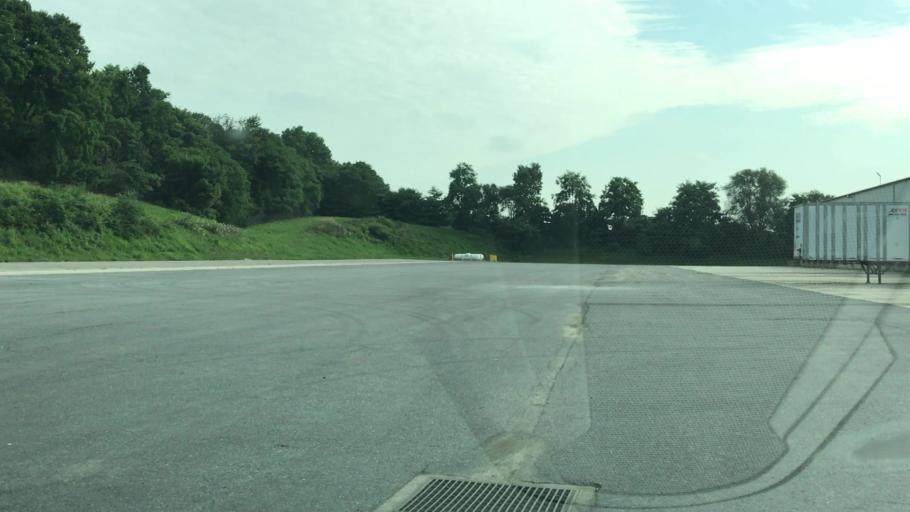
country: US
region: Pennsylvania
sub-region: Franklin County
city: State Line
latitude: 39.7184
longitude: -77.7209
